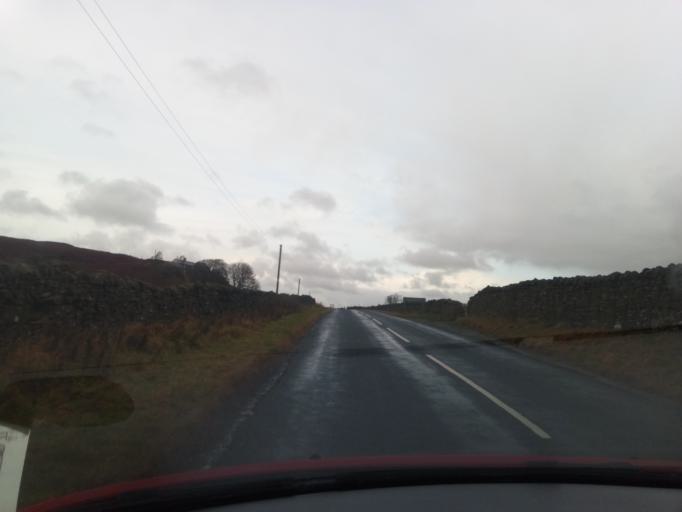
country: GB
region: England
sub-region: County Durham
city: Muggleswick
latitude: 54.8483
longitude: -1.9800
